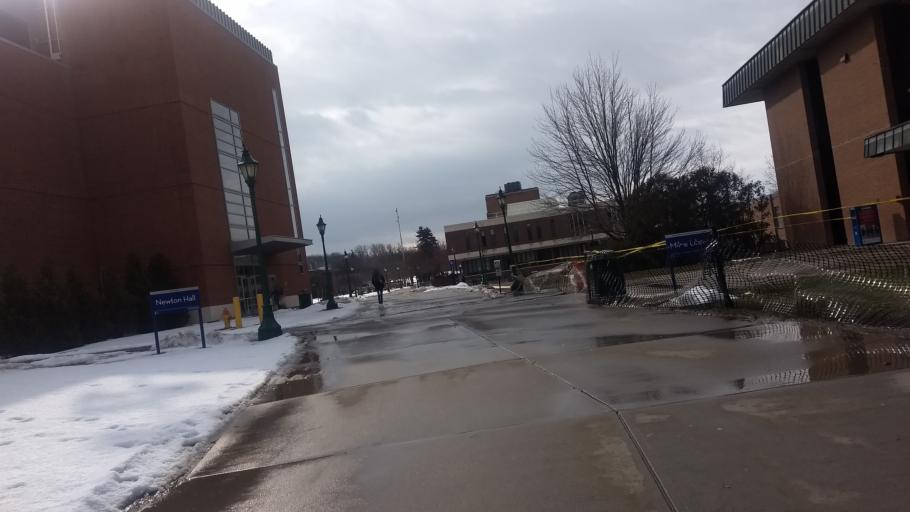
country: US
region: New York
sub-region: Livingston County
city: Geneseo
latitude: 42.7975
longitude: -77.8194
